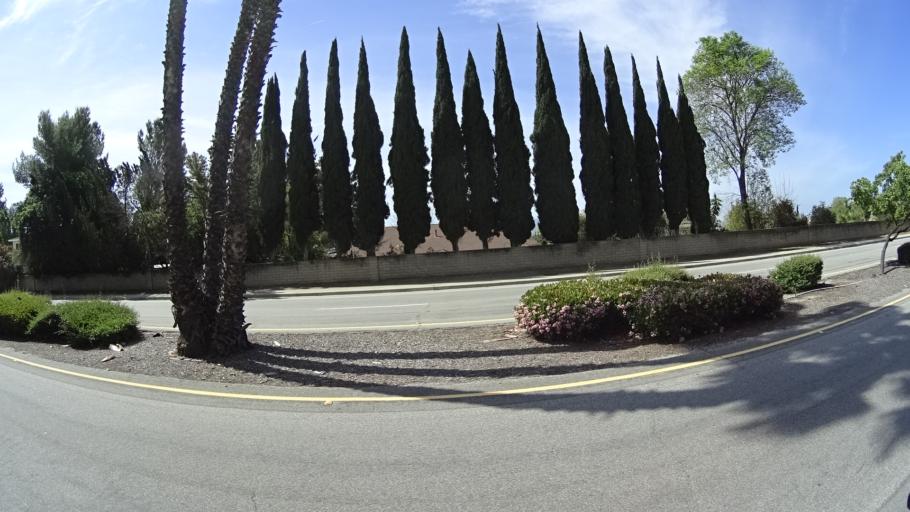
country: US
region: California
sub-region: Ventura County
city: Moorpark
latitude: 34.2319
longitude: -118.8573
